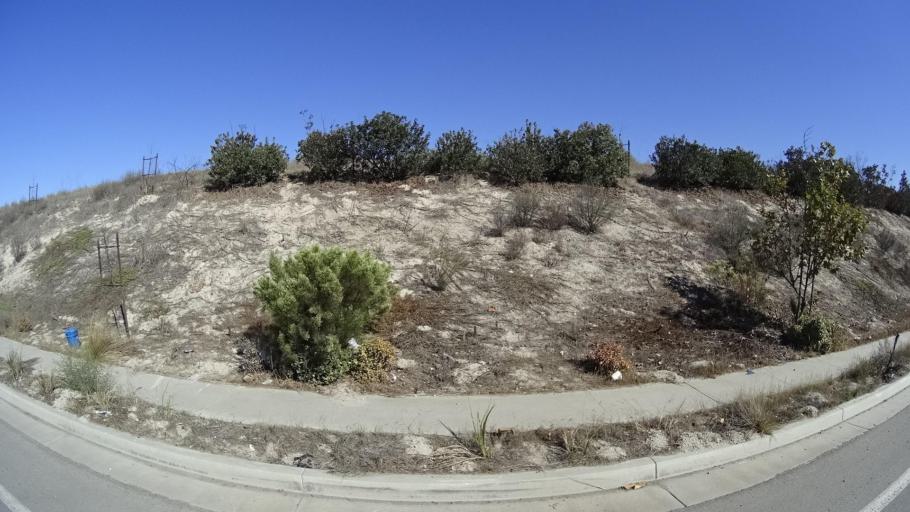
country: MX
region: Baja California
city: Tijuana
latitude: 32.5602
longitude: -116.9328
